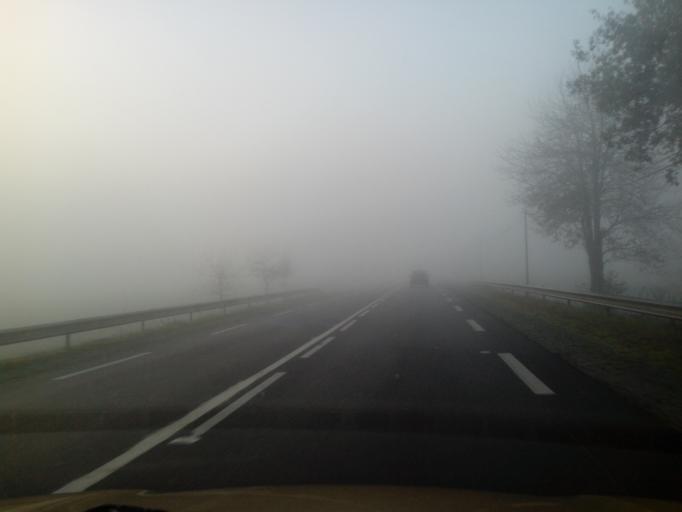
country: FR
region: Brittany
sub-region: Departement du Morbihan
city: Mauron
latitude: 48.0645
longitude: -2.2907
